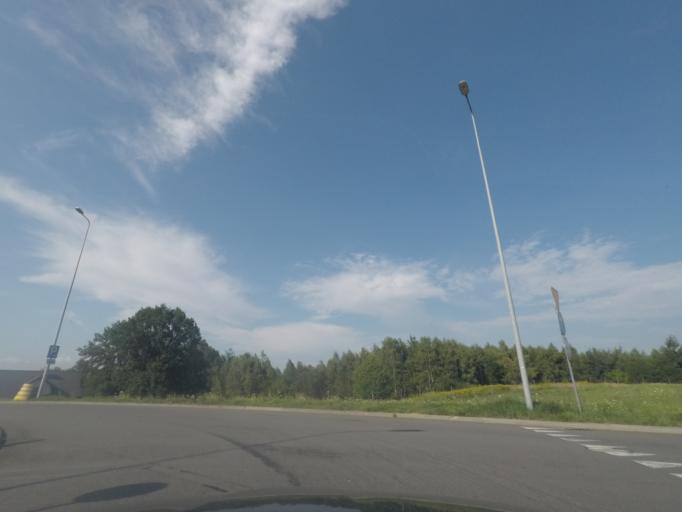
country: PL
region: Silesian Voivodeship
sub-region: Powiat wodzislawski
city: Mszana
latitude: 49.9615
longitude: 18.5275
